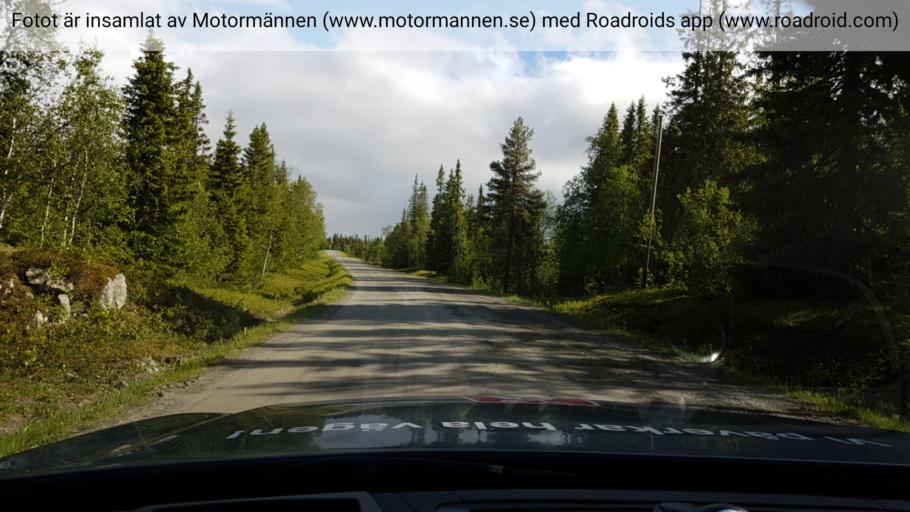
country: NO
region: Nord-Trondelag
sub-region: Snasa
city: Snaase
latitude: 63.7356
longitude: 12.4675
